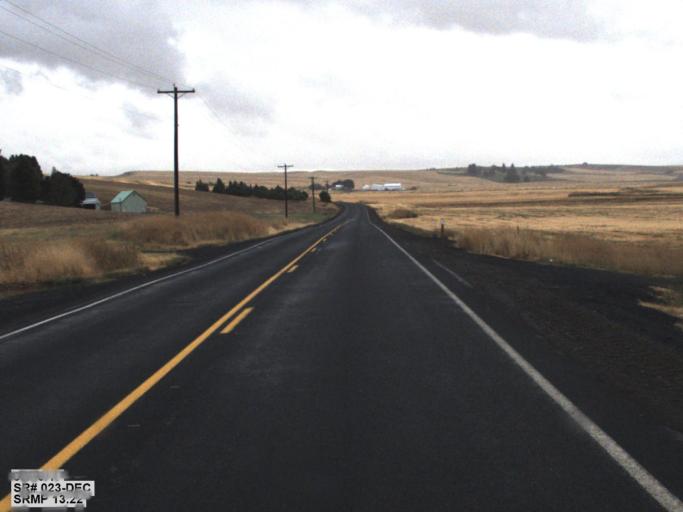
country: US
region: Washington
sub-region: Whitman County
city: Colfax
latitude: 47.0884
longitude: -117.5624
